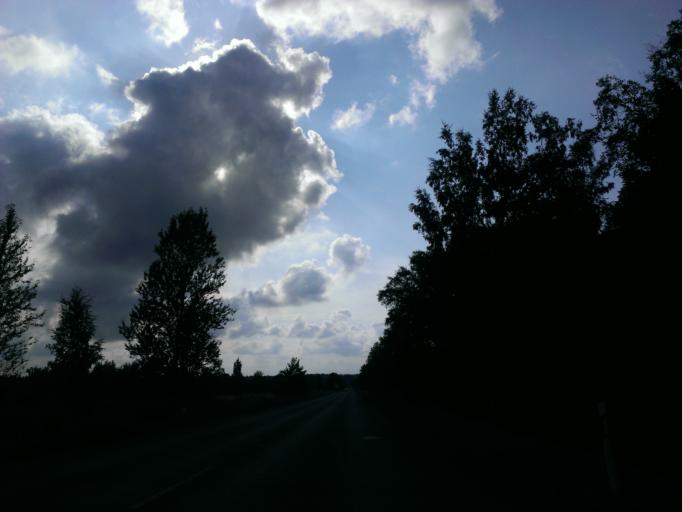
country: LV
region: Priekuli
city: Priekuli
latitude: 57.2942
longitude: 25.4561
